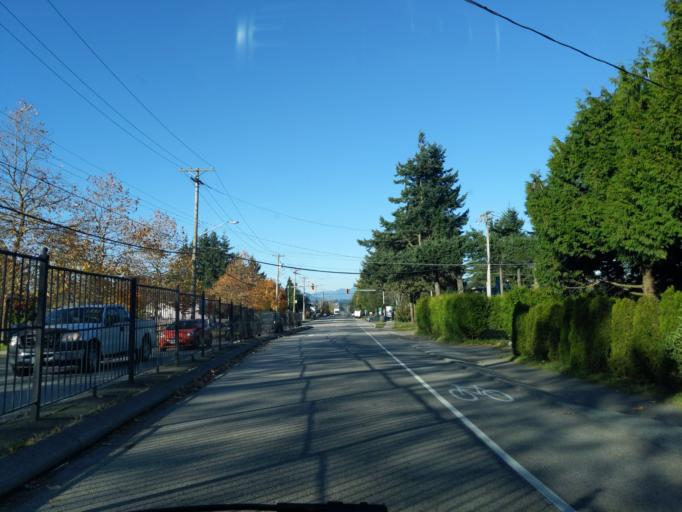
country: CA
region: British Columbia
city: New Westminster
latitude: 49.1923
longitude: -122.8564
